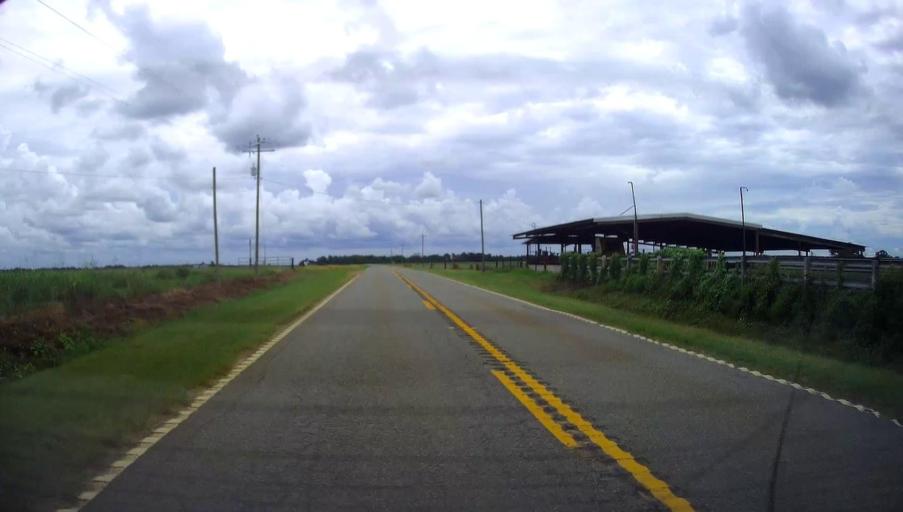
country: US
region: Georgia
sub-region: Dooly County
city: Unadilla
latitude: 32.2703
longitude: -83.8143
